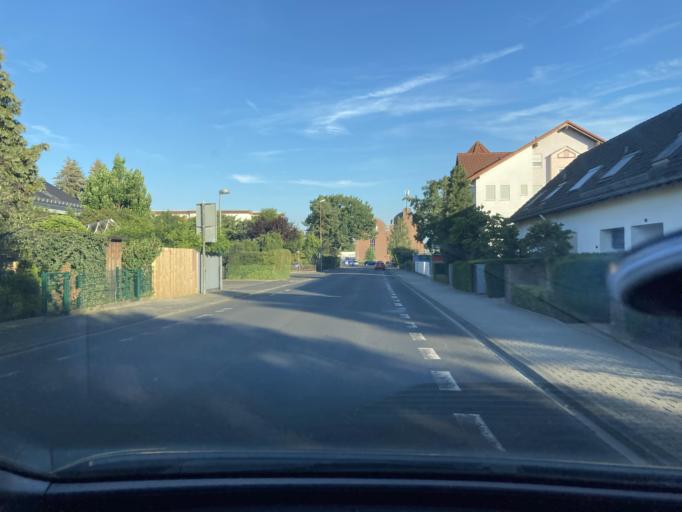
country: DE
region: Hesse
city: Heusenstamm
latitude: 50.0525
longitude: 8.7966
